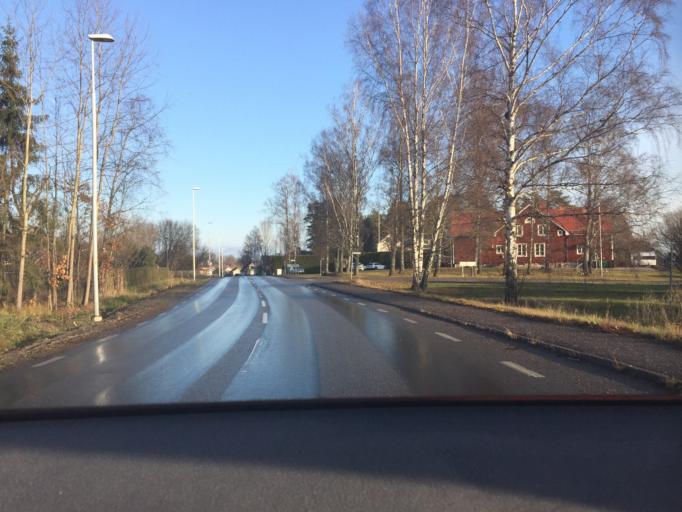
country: SE
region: OEstergoetland
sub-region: Norrkopings Kommun
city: Krokek
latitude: 58.5739
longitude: 16.5555
